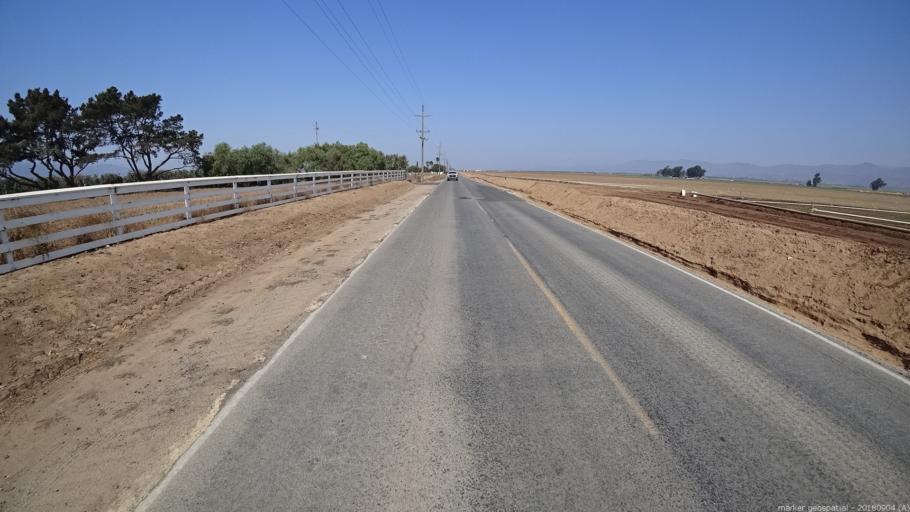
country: US
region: California
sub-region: Monterey County
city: Chualar
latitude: 36.5504
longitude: -121.4732
